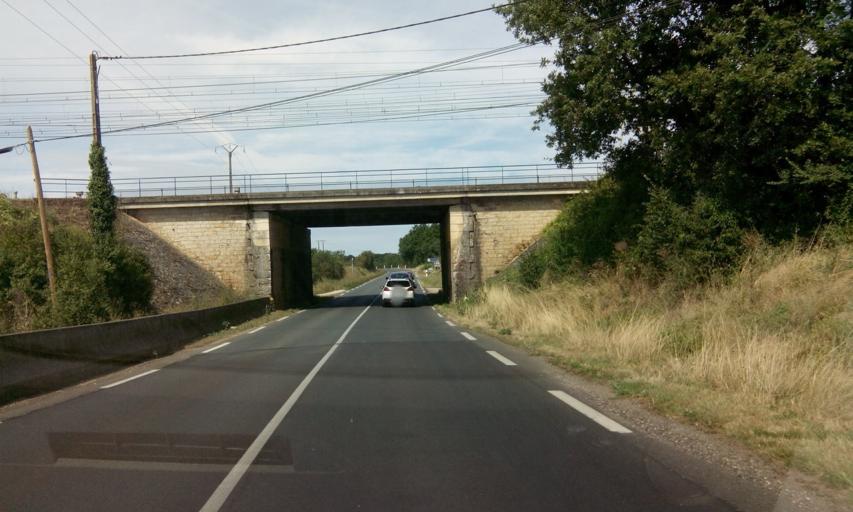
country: FR
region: Poitou-Charentes
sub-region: Departement de la Vienne
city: Civray
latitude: 46.1421
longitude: 0.2177
